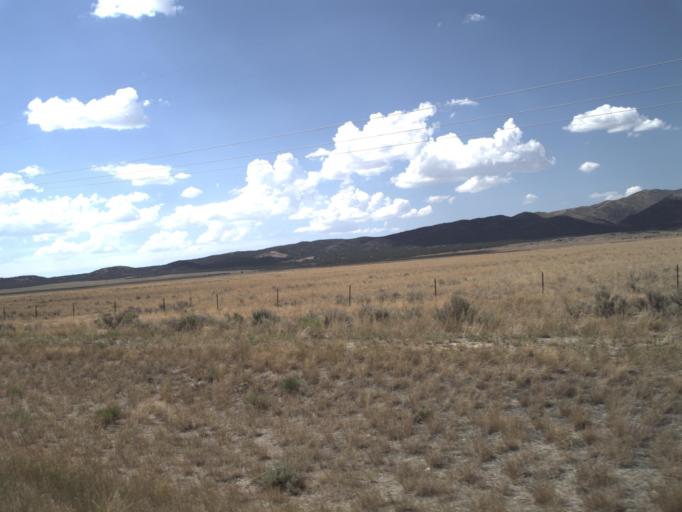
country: US
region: Idaho
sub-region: Power County
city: American Falls
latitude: 41.9679
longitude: -113.0921
